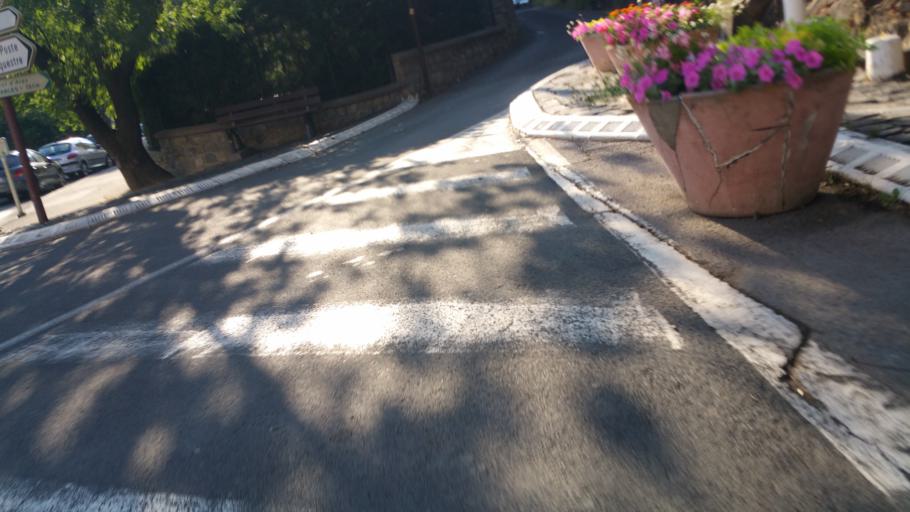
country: FR
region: Languedoc-Roussillon
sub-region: Departement des Pyrenees-Orientales
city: els Banys d'Arles
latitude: 42.4745
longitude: 2.6707
